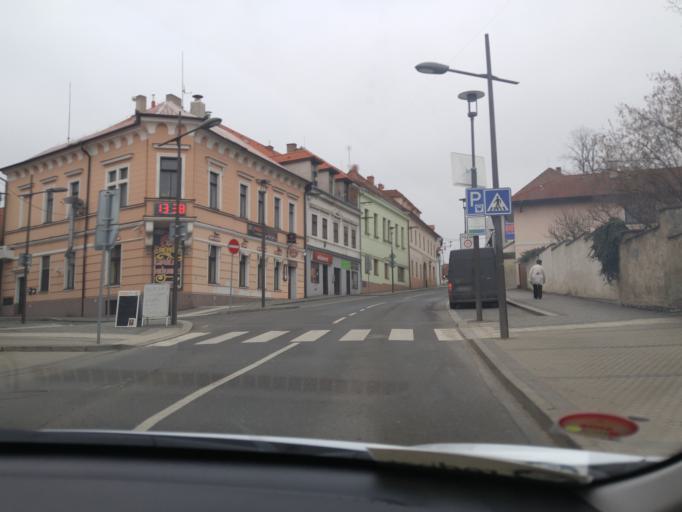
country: CZ
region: Central Bohemia
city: Brandys nad Labem-Stara Boleslav
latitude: 50.1872
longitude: 14.6577
